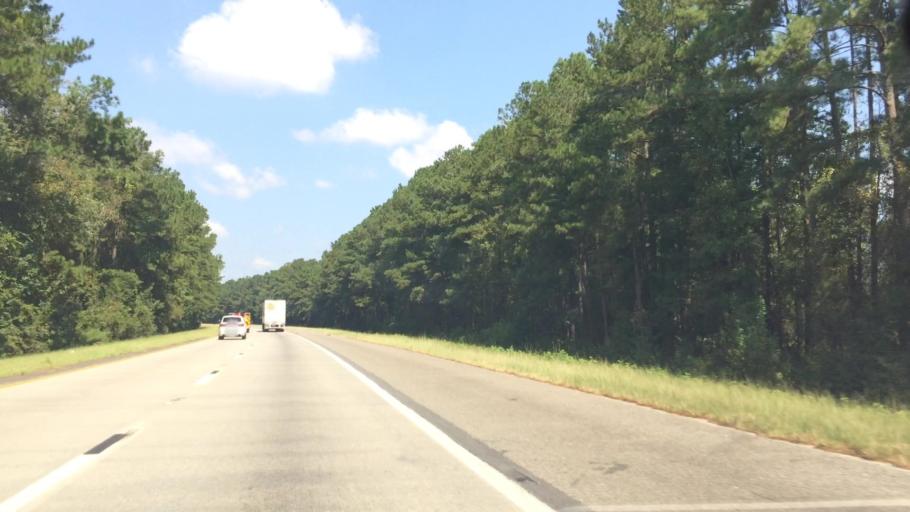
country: US
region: South Carolina
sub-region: Colleton County
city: Walterboro
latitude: 33.0196
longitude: -80.6654
